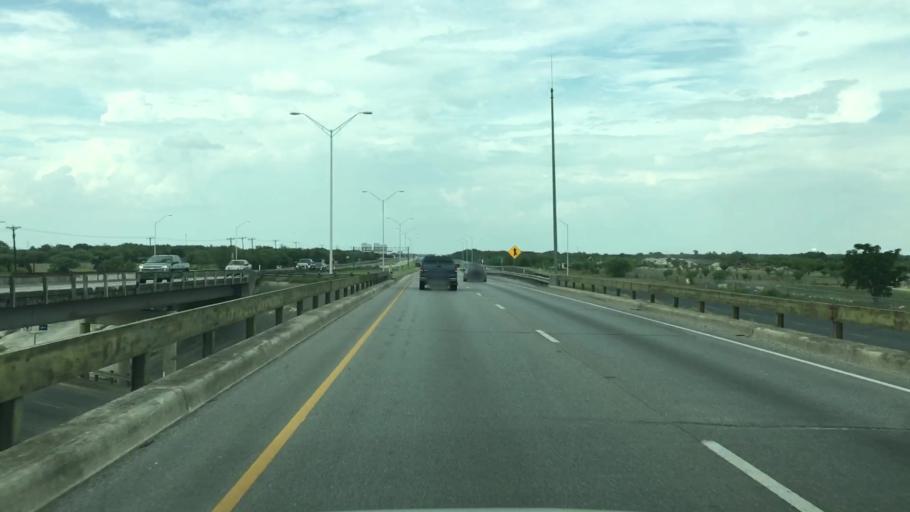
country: US
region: Texas
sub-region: Bexar County
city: China Grove
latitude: 29.3529
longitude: -98.4003
